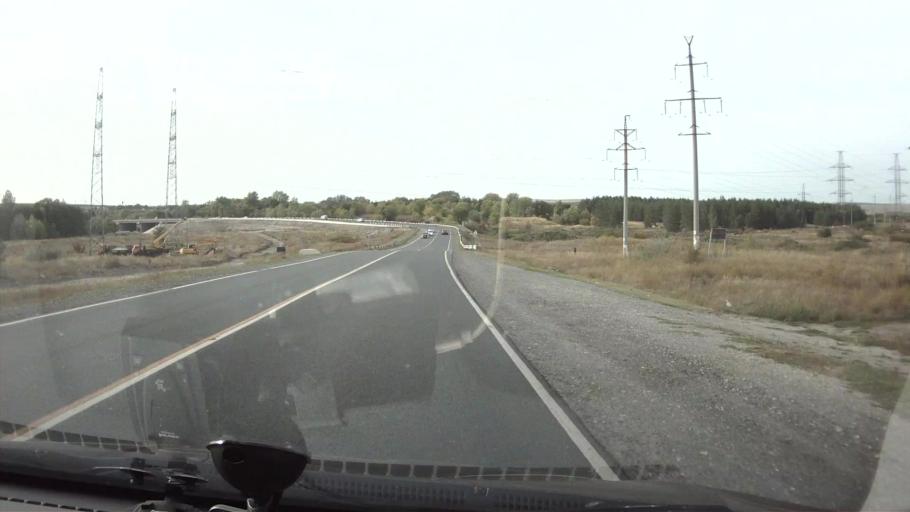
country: RU
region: Saratov
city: Sennoy
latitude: 52.1426
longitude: 46.9097
